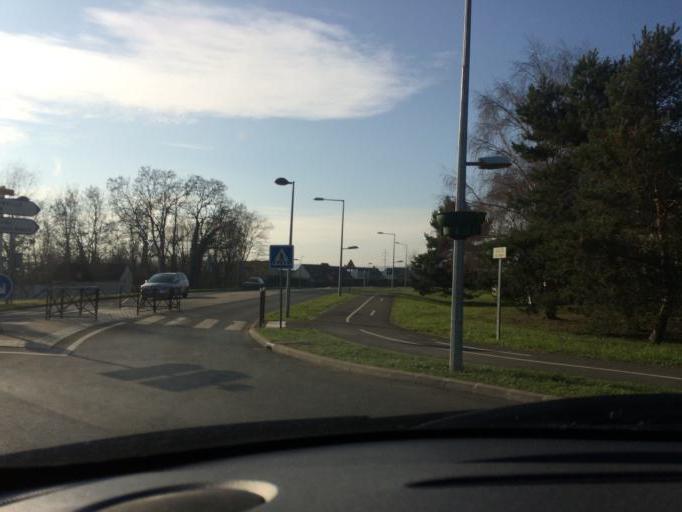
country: FR
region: Ile-de-France
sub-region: Departement de l'Essonne
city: Bouray-sur-Juine
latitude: 48.5284
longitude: 2.2969
